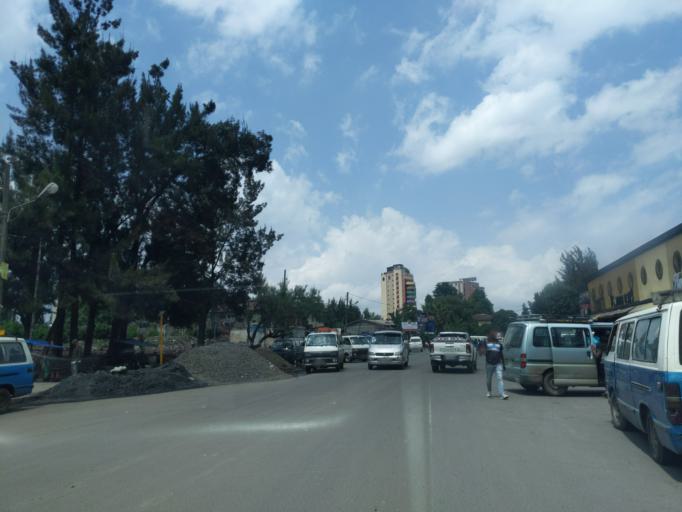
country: ET
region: Adis Abeba
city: Addis Ababa
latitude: 9.0159
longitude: 38.7705
